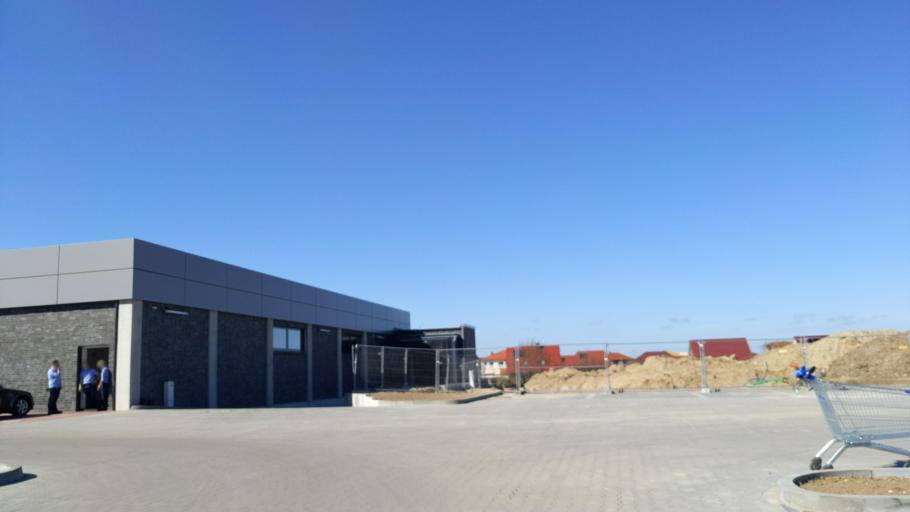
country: DE
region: Schleswig-Holstein
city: Neustadt in Holstein
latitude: 54.1044
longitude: 10.8356
